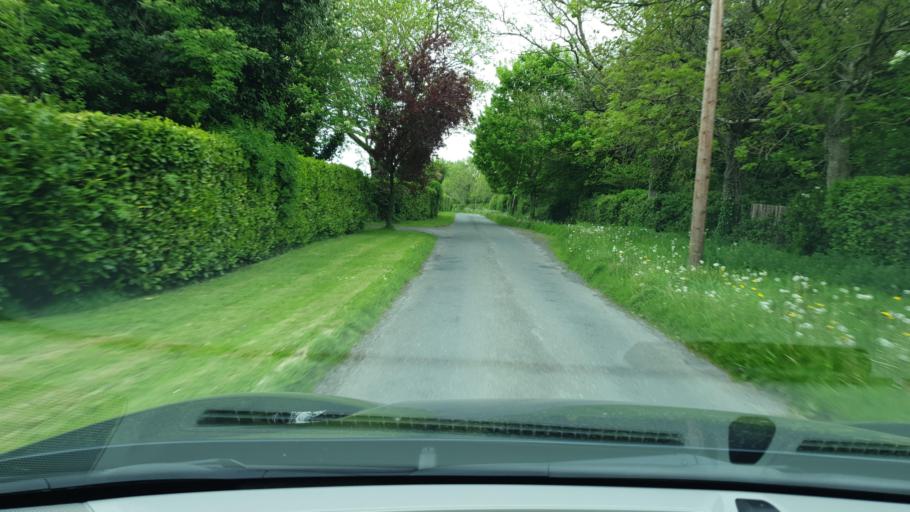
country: IE
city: Confey
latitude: 53.4108
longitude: -6.5258
